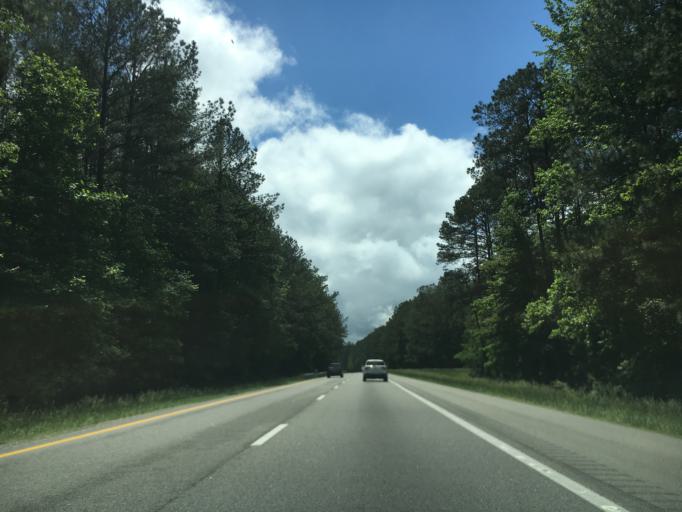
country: US
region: Virginia
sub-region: Brunswick County
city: Lawrenceville
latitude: 36.8216
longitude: -77.9615
